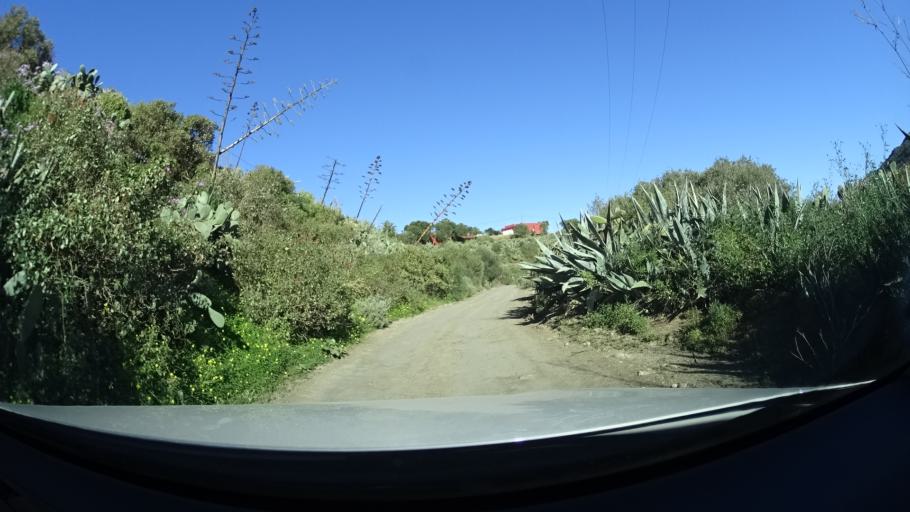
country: ES
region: Canary Islands
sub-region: Provincia de Las Palmas
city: Santa Brigida
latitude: 28.0321
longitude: -15.4605
